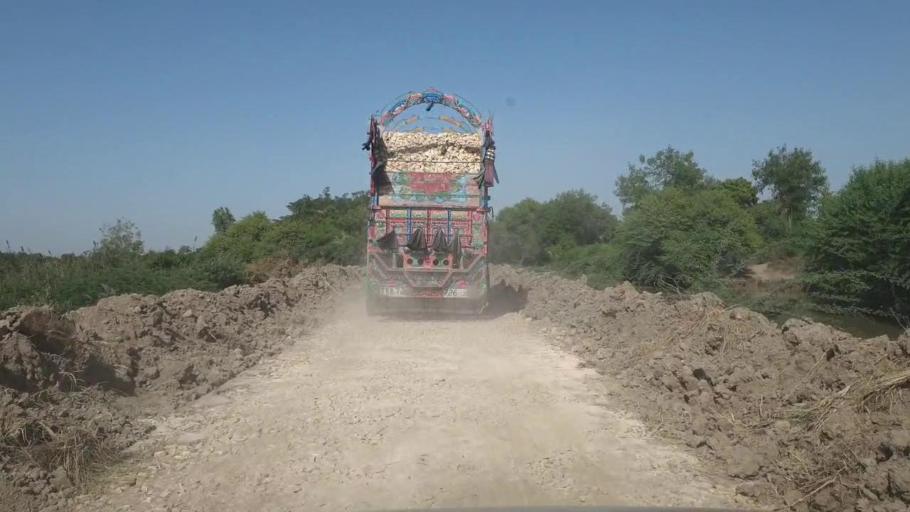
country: PK
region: Sindh
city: Kadhan
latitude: 24.5301
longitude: 69.0004
